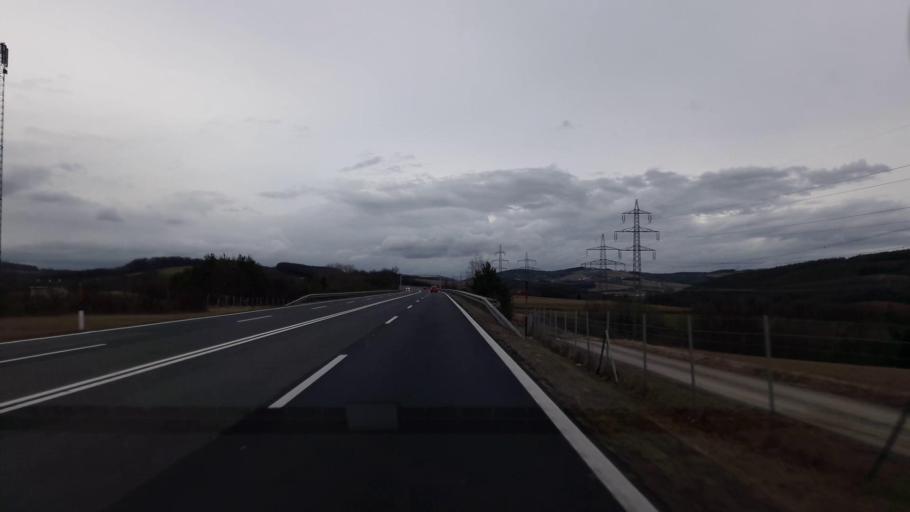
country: AT
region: Burgenland
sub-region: Politischer Bezirk Oberpullendorf
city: Kobersdorf
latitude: 47.6146
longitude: 16.3911
